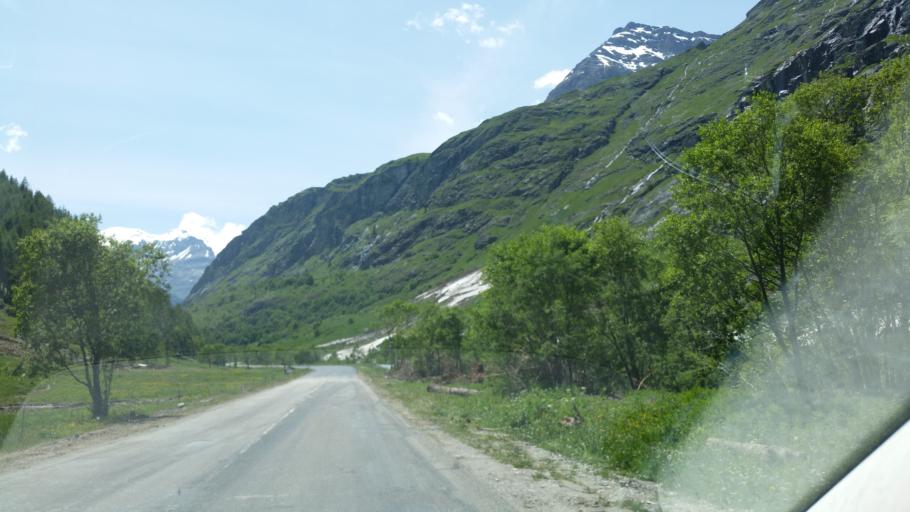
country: FR
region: Rhone-Alpes
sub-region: Departement de la Savoie
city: Val-d'Isere
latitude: 45.3609
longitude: 7.0330
